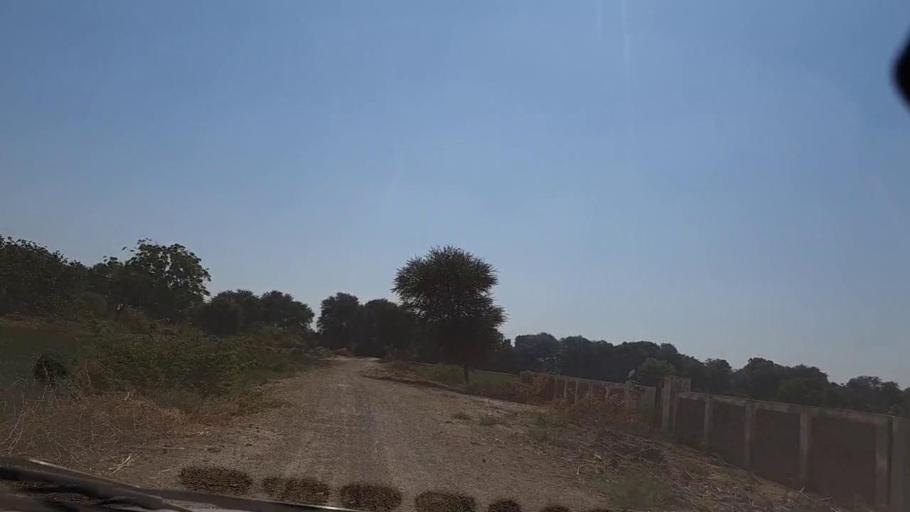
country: PK
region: Sindh
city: Mirpur Khas
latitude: 25.4271
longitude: 69.0559
